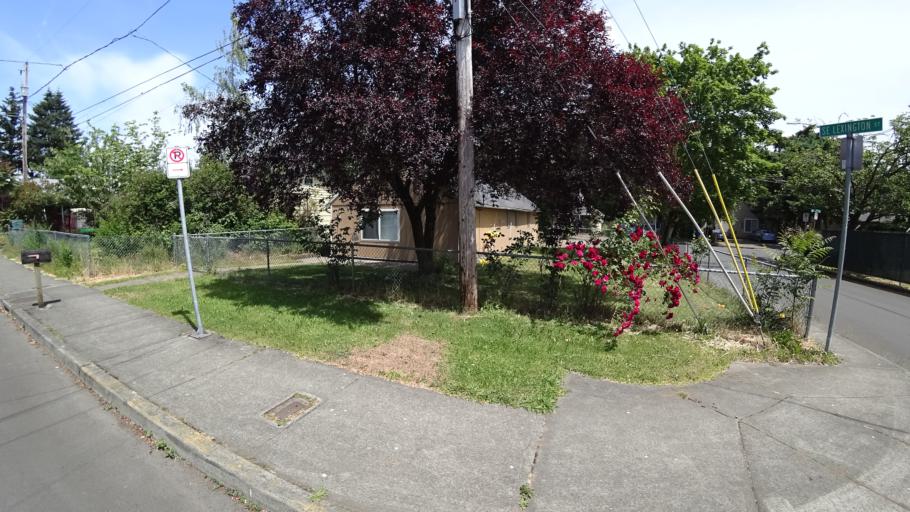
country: US
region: Oregon
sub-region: Multnomah County
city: Lents
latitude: 45.4663
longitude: -122.5949
